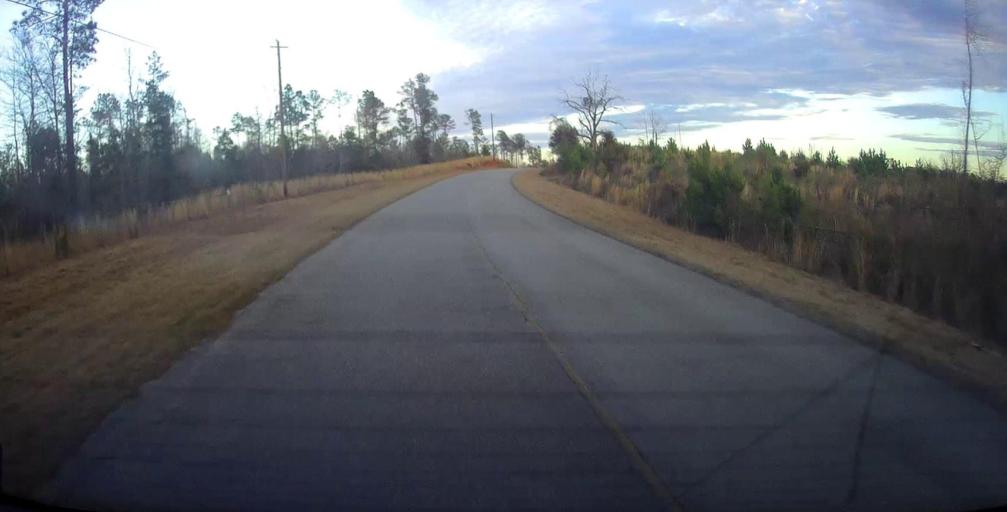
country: US
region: Georgia
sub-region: Harris County
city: Hamilton
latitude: 32.6154
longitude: -84.8321
